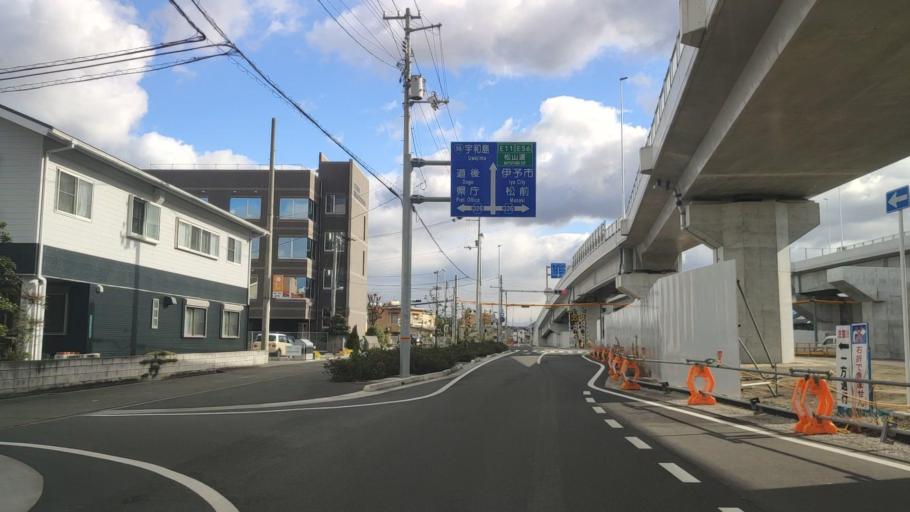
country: JP
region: Ehime
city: Masaki-cho
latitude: 33.8115
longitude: 132.7298
